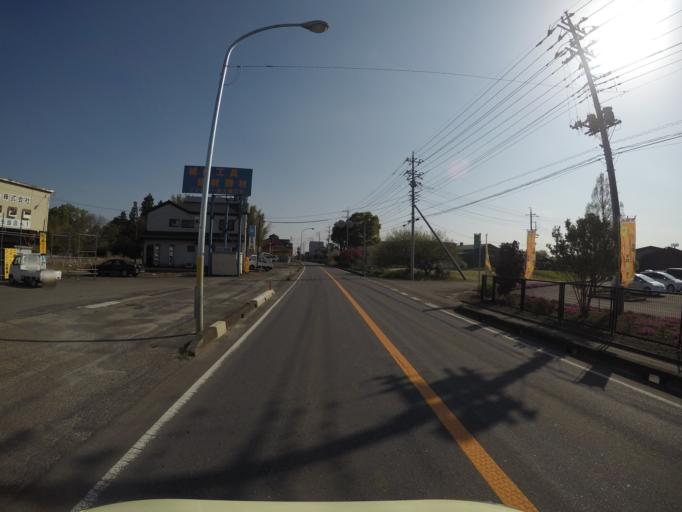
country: JP
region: Ibaraki
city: Yuki
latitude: 36.2821
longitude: 139.8795
